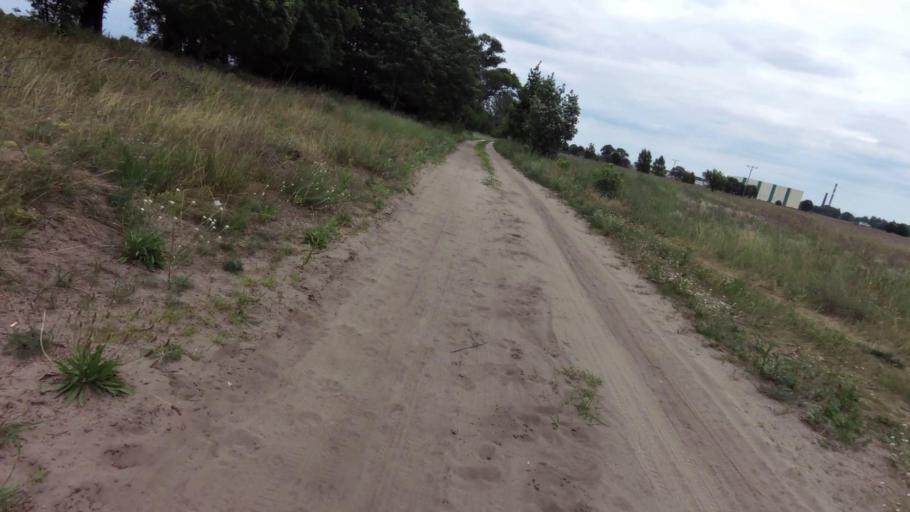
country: PL
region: Lubusz
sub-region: Powiat gorzowski
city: Kostrzyn nad Odra
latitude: 52.6123
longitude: 14.6087
